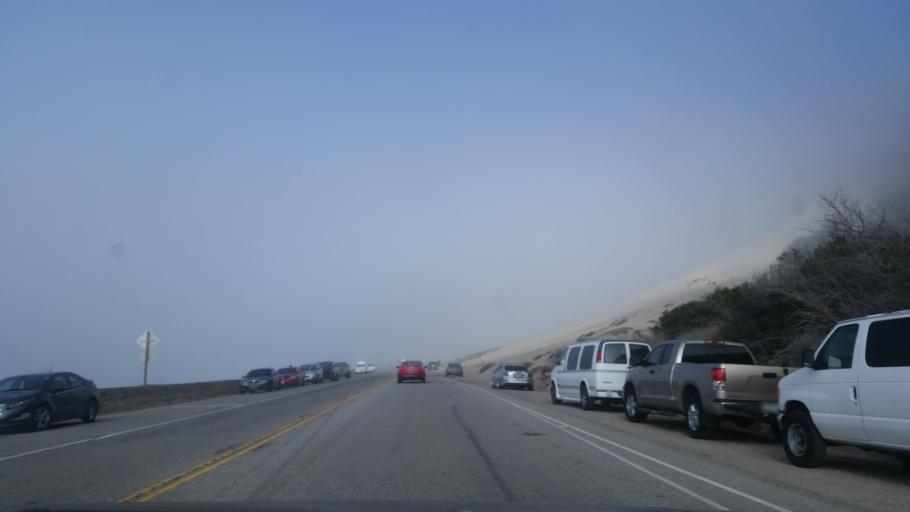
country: US
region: California
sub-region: Ventura County
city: Casa Conejo
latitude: 34.0731
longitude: -119.0187
